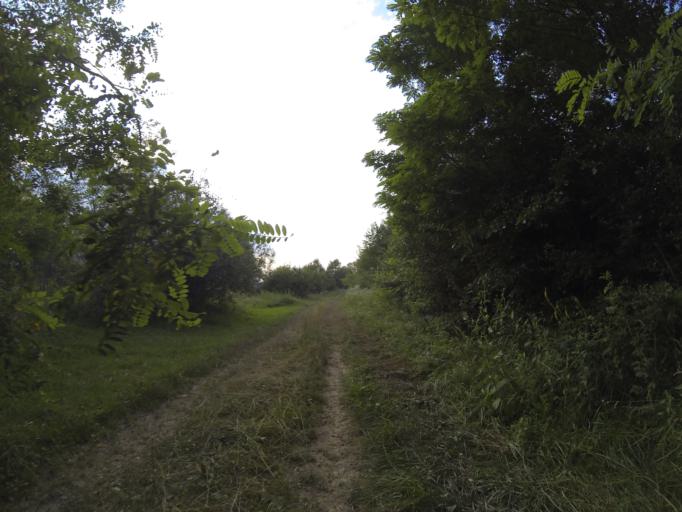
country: RO
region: Brasov
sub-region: Comuna Sinca Noua
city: Sinca Noua
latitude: 45.7173
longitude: 25.2509
